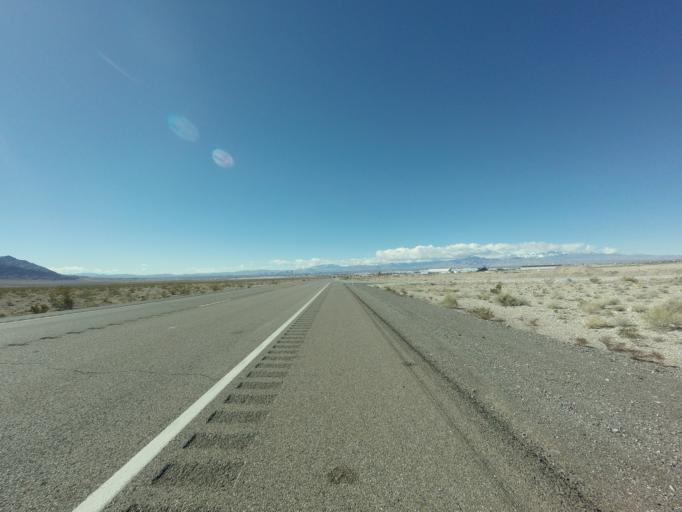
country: US
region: Nevada
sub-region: Clark County
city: Nellis Air Force Base
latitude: 36.2787
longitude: -114.9892
